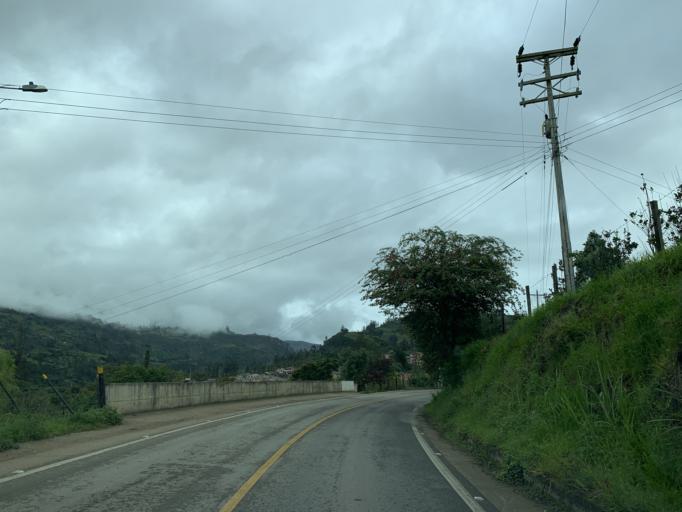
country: CO
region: Boyaca
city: Tibana
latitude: 5.3235
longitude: -73.3942
